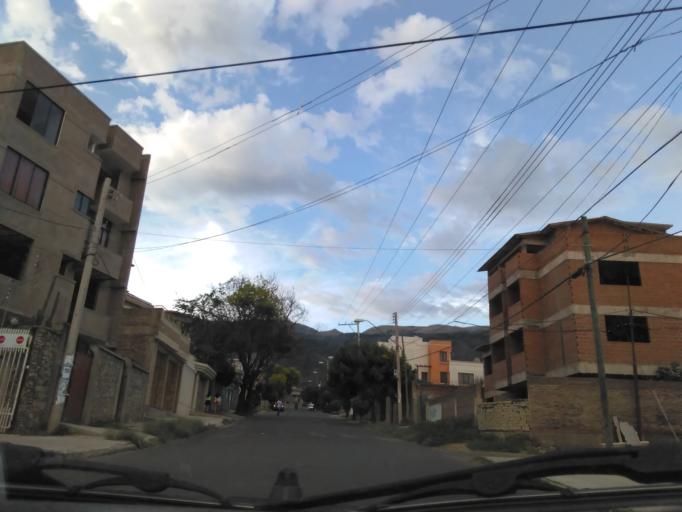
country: BO
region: Cochabamba
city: Cochabamba
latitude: -17.3684
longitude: -66.1532
